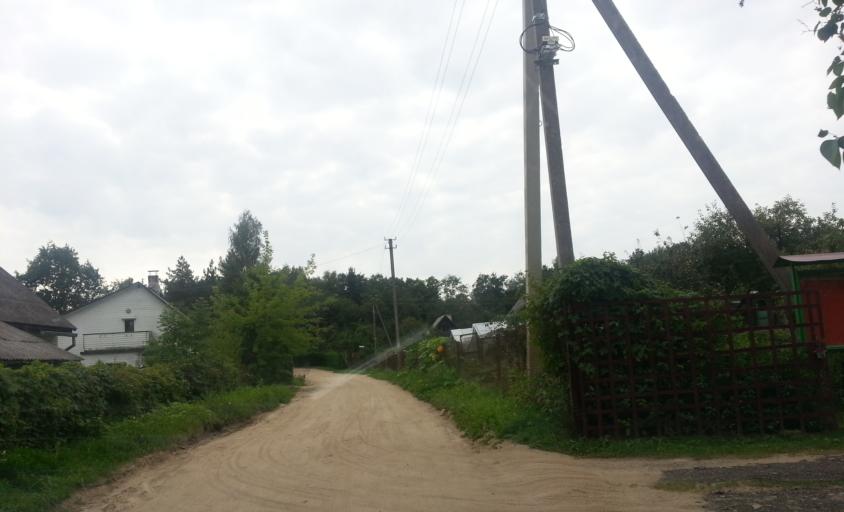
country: LT
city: Grigiskes
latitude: 54.7588
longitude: 25.0216
